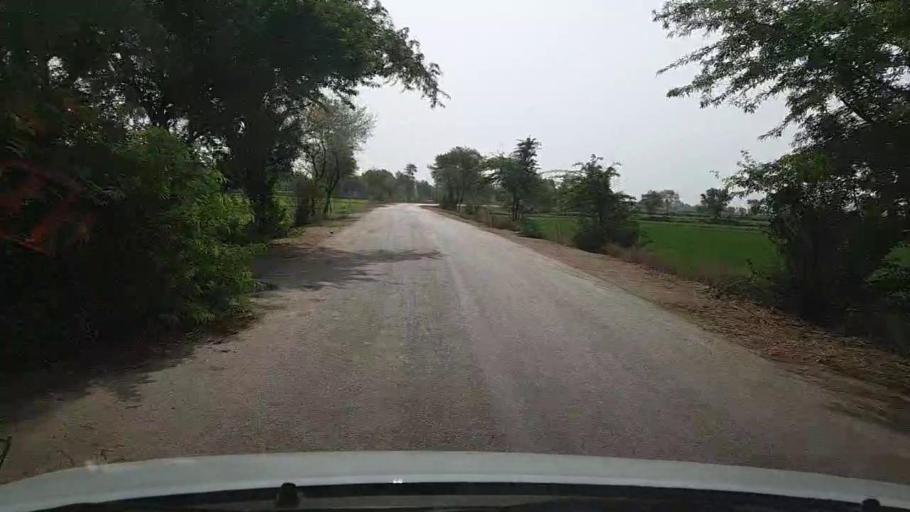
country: PK
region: Sindh
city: Mehar
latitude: 27.1190
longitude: 67.8311
